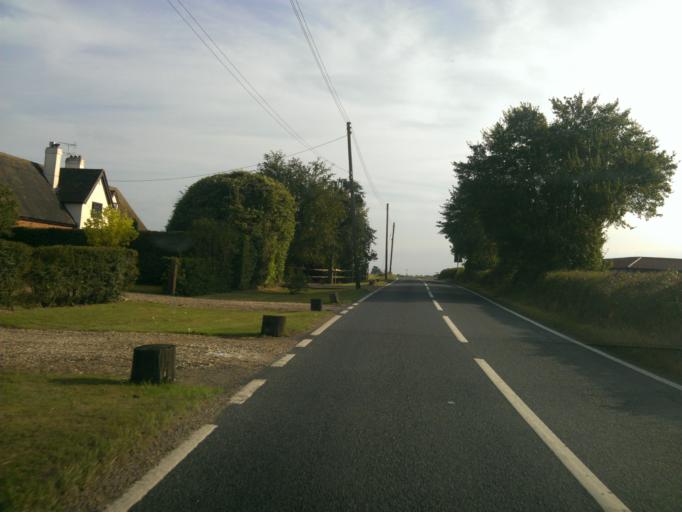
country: GB
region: England
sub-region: Essex
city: Witham
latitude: 51.8347
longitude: 0.6487
